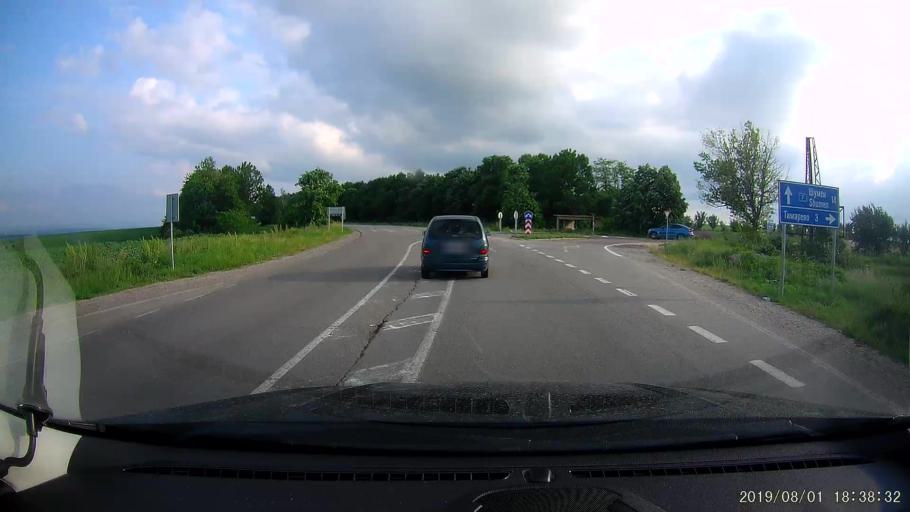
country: BG
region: Shumen
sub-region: Obshtina Khitrino
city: Gara Khitrino
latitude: 43.4006
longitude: 26.9160
